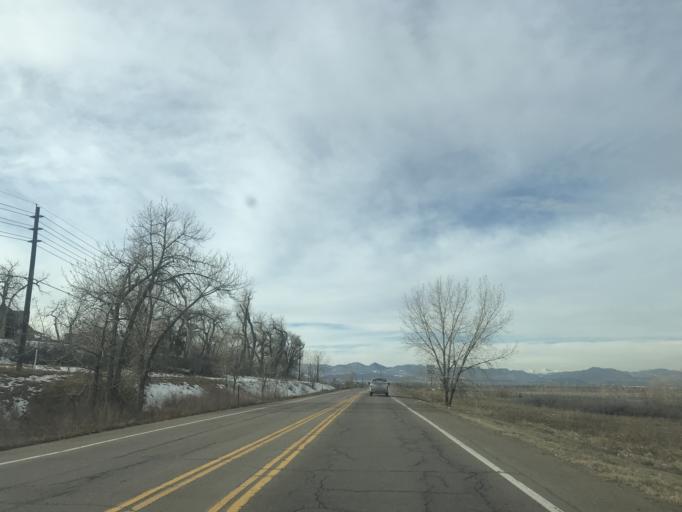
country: US
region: Colorado
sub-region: Arapahoe County
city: Columbine Valley
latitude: 39.5656
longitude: -105.0131
